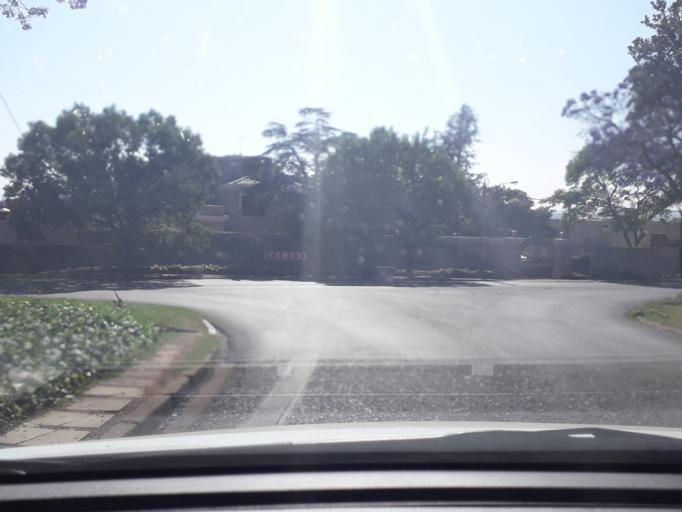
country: ZA
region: Gauteng
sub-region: City of Johannesburg Metropolitan Municipality
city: Johannesburg
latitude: -26.1430
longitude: 27.9751
